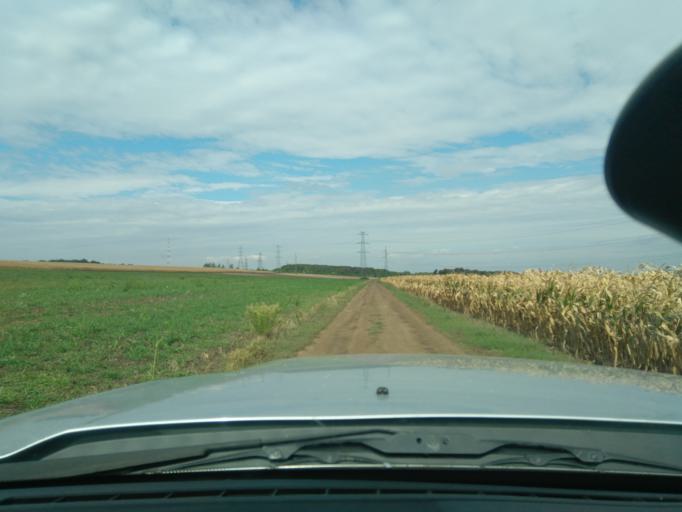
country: HU
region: Fejer
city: Val
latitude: 47.3714
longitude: 18.6974
